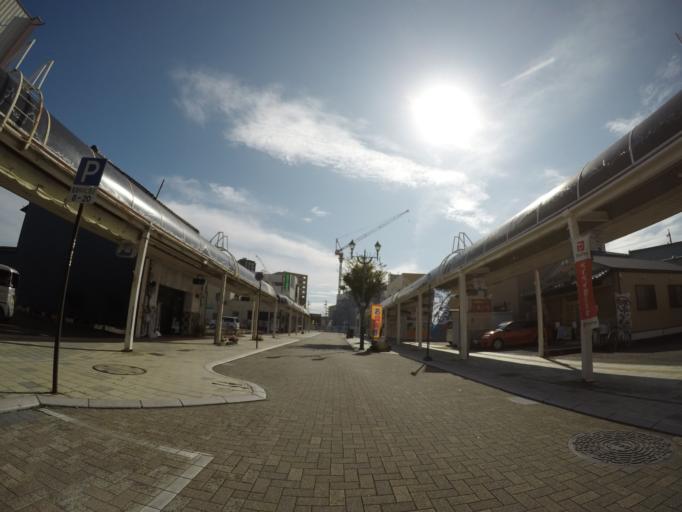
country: JP
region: Shizuoka
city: Yaizu
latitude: 34.8694
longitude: 138.3204
